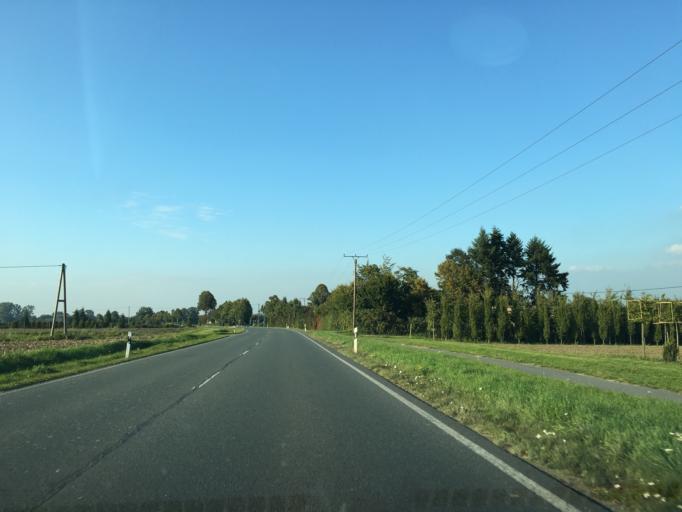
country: DE
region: North Rhine-Westphalia
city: Ludinghausen
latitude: 51.7715
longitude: 7.3858
